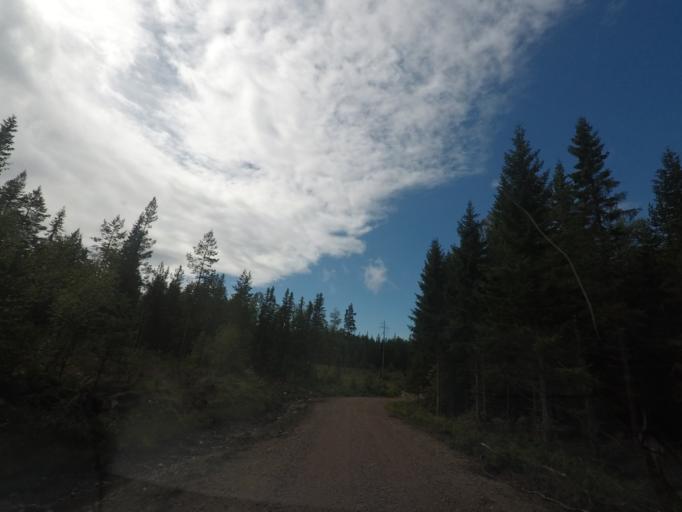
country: SE
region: Vaermland
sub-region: Filipstads Kommun
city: Lesjofors
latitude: 60.0952
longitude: 14.3836
